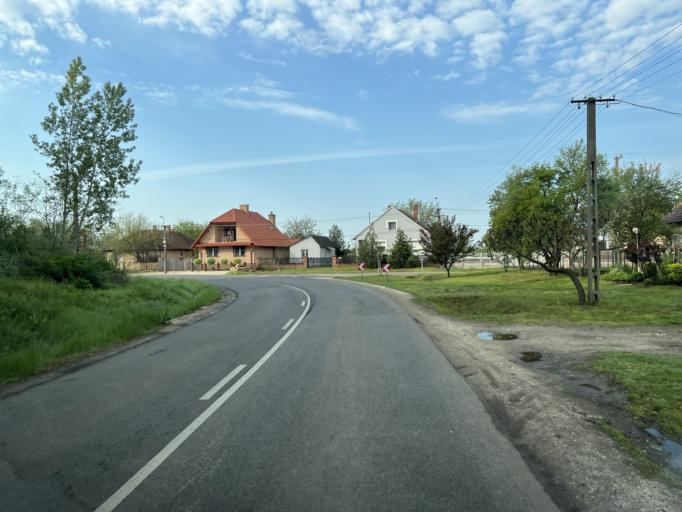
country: HU
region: Pest
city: Abony
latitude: 47.2050
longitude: 20.0092
